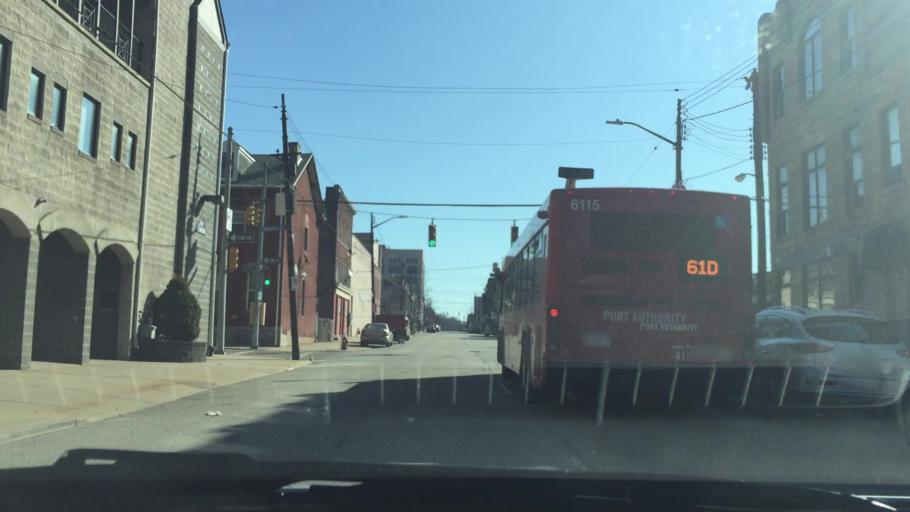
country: US
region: Pennsylvania
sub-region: Allegheny County
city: Pittsburgh
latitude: 40.4376
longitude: -79.9846
